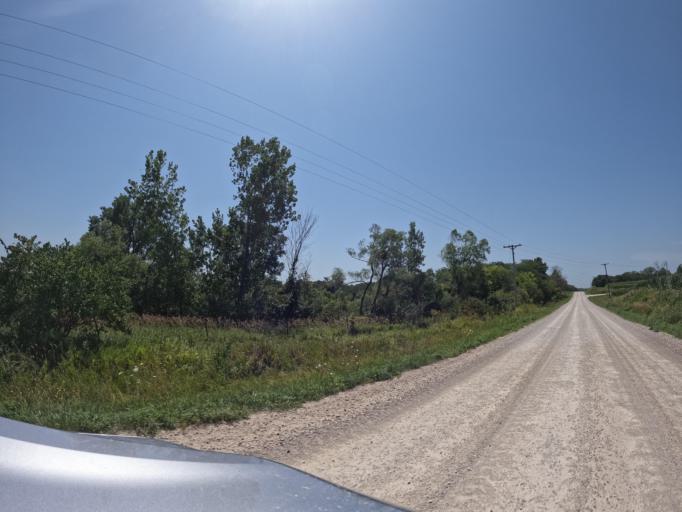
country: US
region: Iowa
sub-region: Henry County
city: Mount Pleasant
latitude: 40.9450
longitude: -91.6584
